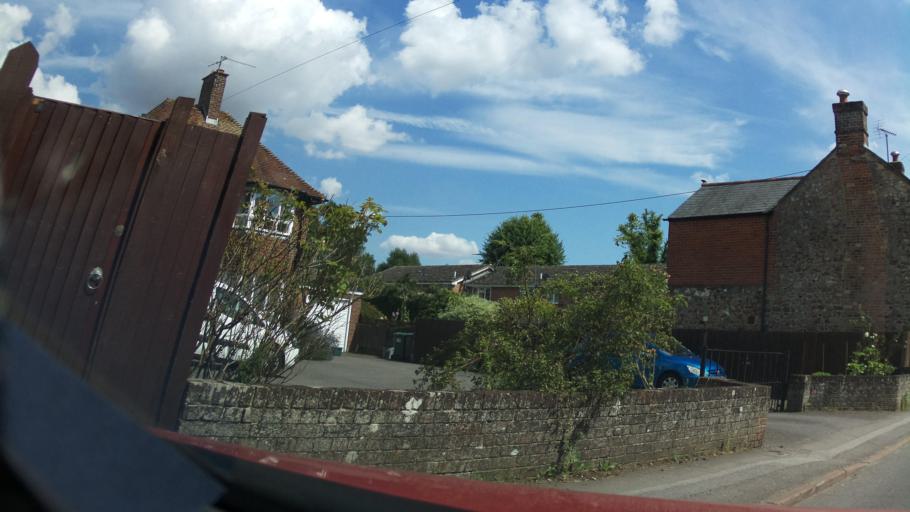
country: GB
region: England
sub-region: West Berkshire
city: Lambourn
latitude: 51.5079
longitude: -1.5299
